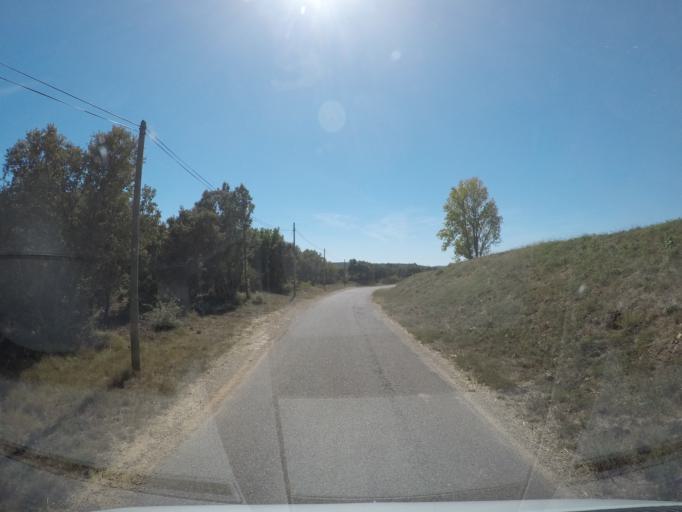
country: FR
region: Languedoc-Roussillon
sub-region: Departement de l'Herault
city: Aniane
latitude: 43.7297
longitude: 3.6492
